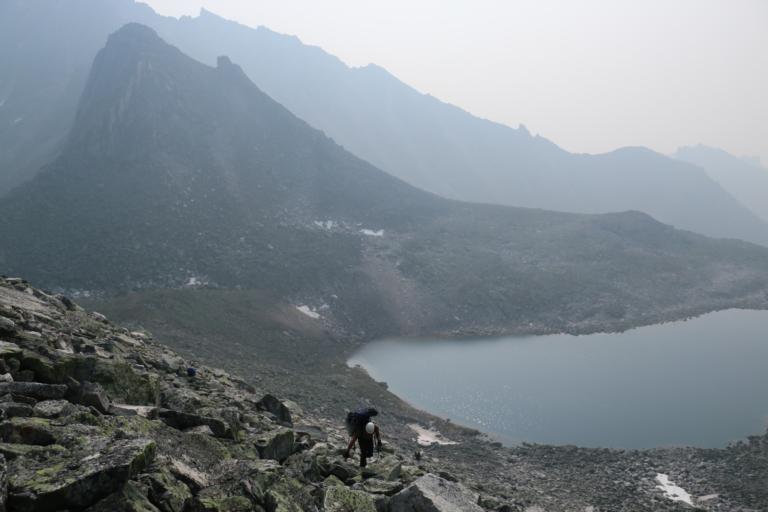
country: RU
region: Respublika Buryatiya
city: Kichera
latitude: 56.2426
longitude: 110.6847
